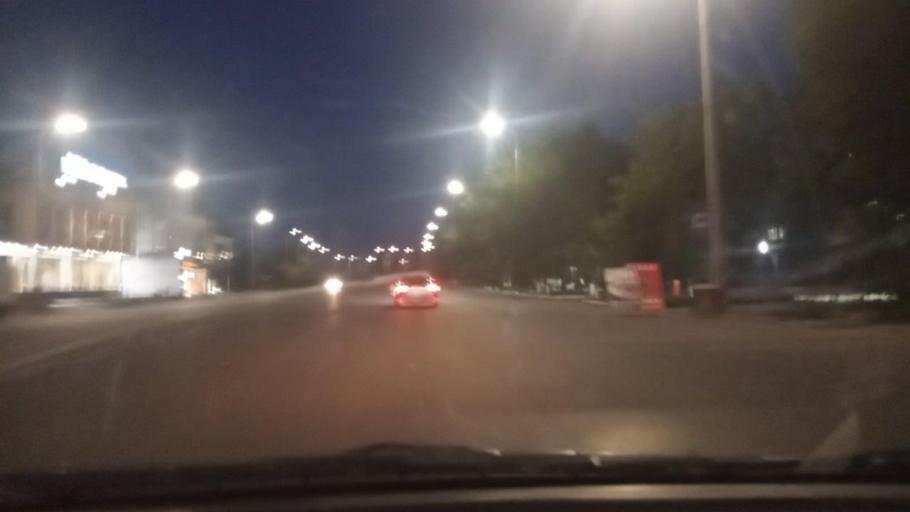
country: UZ
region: Toshkent Shahri
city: Tashkent
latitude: 41.2625
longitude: 69.2324
